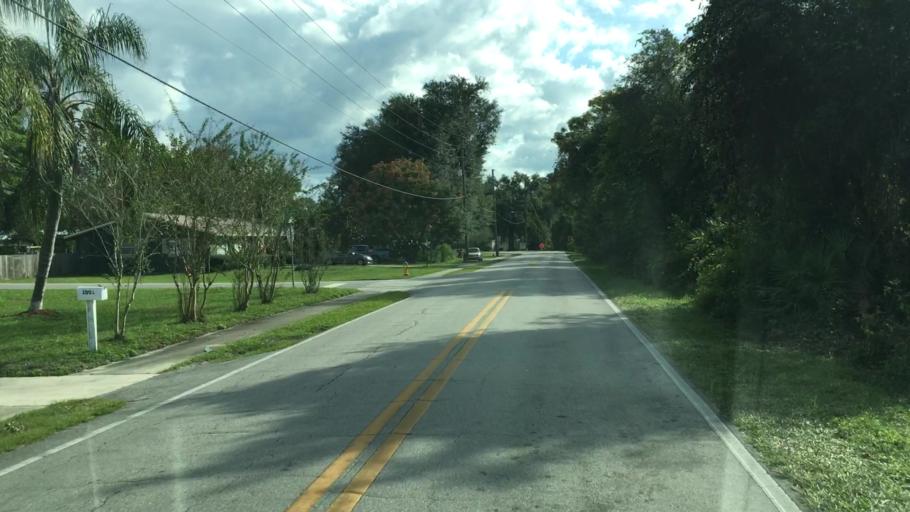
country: US
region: Florida
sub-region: Volusia County
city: North DeLand
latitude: 29.0678
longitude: -81.2713
